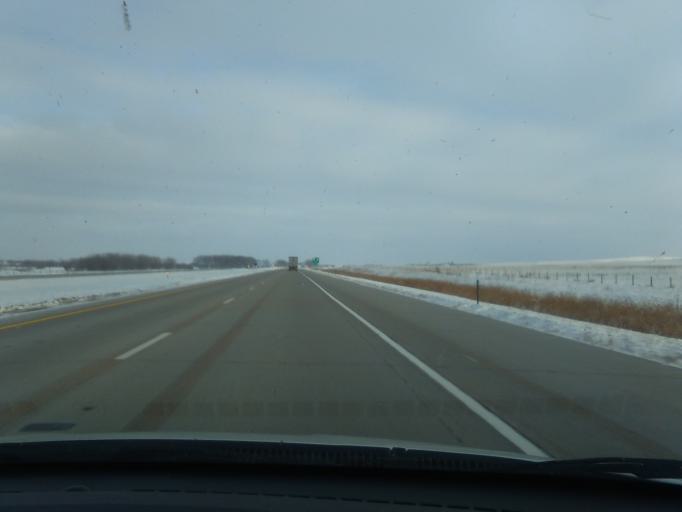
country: US
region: Nebraska
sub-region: Deuel County
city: Chappell
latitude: 41.0875
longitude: -102.5018
